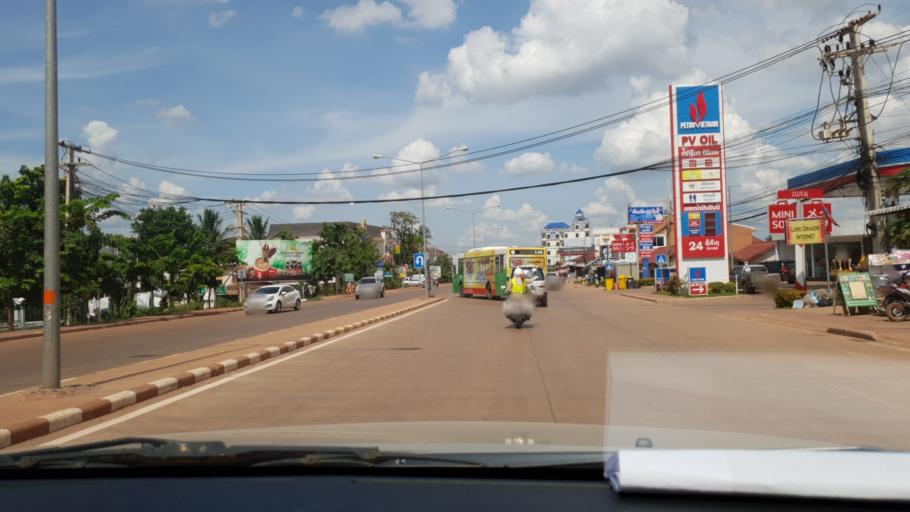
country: LA
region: Vientiane
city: Vientiane
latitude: 18.0330
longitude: 102.6397
